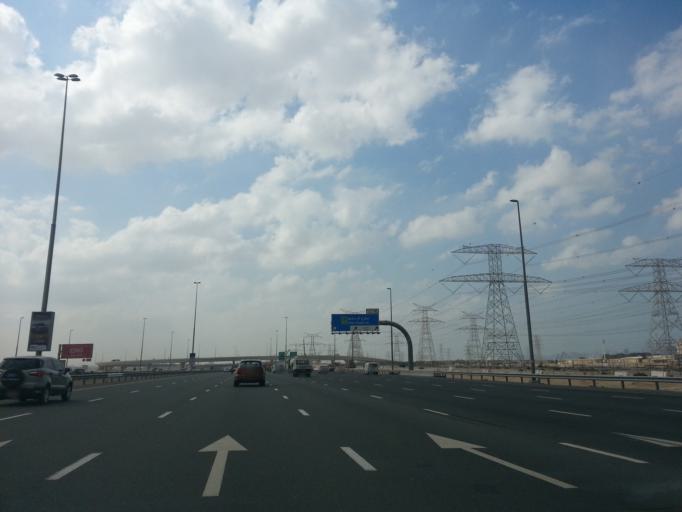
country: AE
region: Dubai
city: Dubai
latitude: 25.1079
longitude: 55.2379
